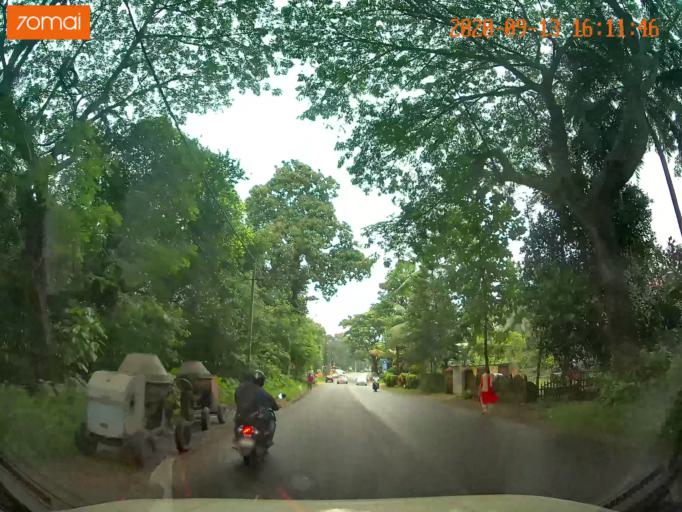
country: IN
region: Kerala
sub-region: Kottayam
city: Palackattumala
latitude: 9.6858
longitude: 76.6139
